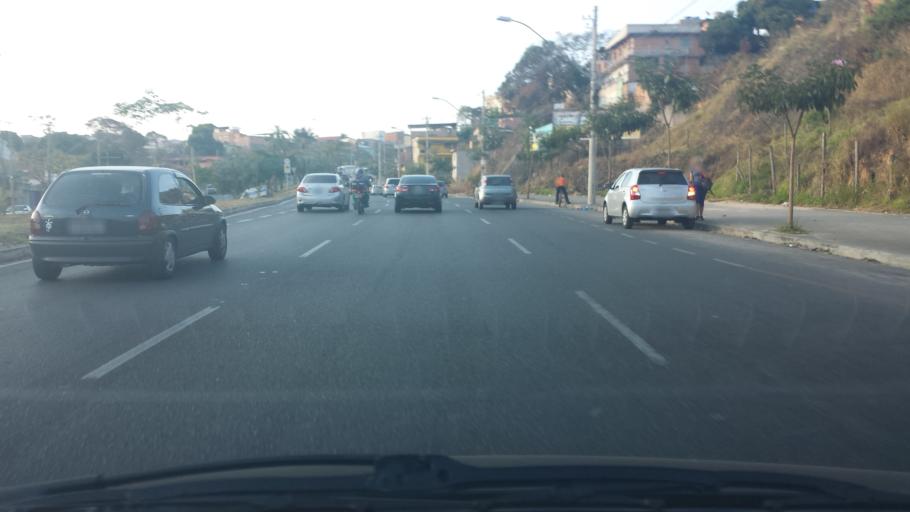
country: BR
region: Minas Gerais
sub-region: Belo Horizonte
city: Belo Horizonte
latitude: -19.8940
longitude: -43.9932
